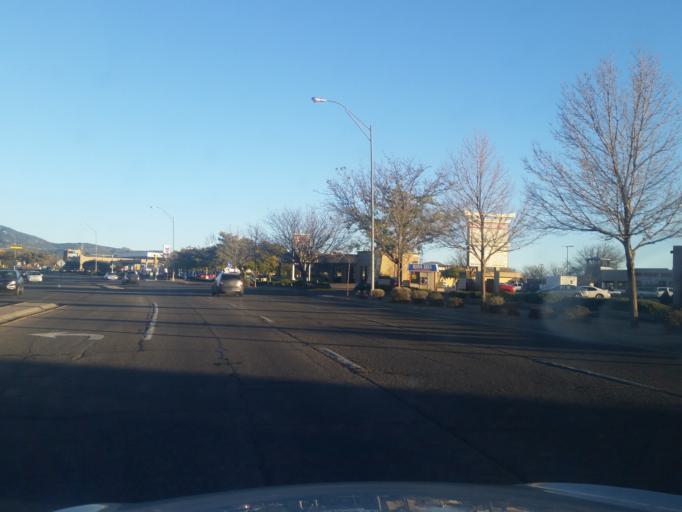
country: US
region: New Mexico
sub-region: Santa Fe County
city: Santa Fe
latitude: 35.6597
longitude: -105.9744
